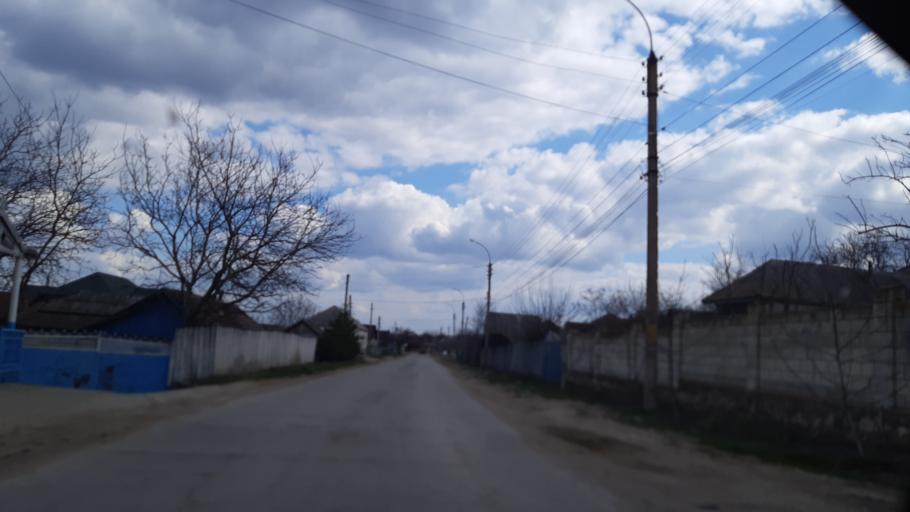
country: MD
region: Laloveni
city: Ialoveni
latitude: 46.8748
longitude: 28.7599
